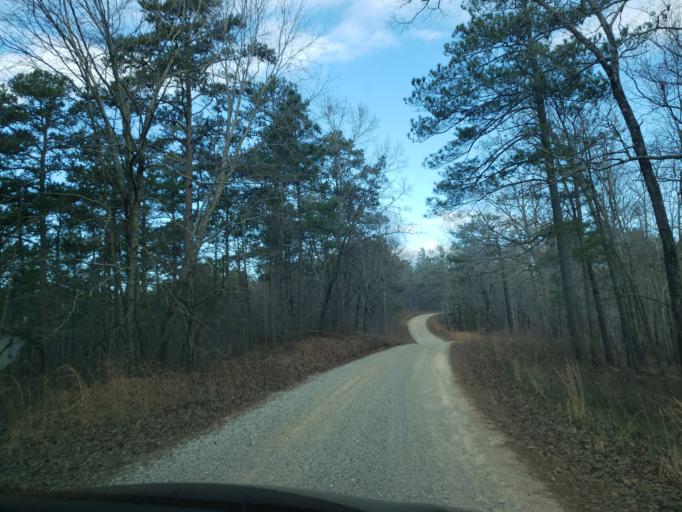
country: US
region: Alabama
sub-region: Cleburne County
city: Heflin
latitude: 33.6651
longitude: -85.6321
